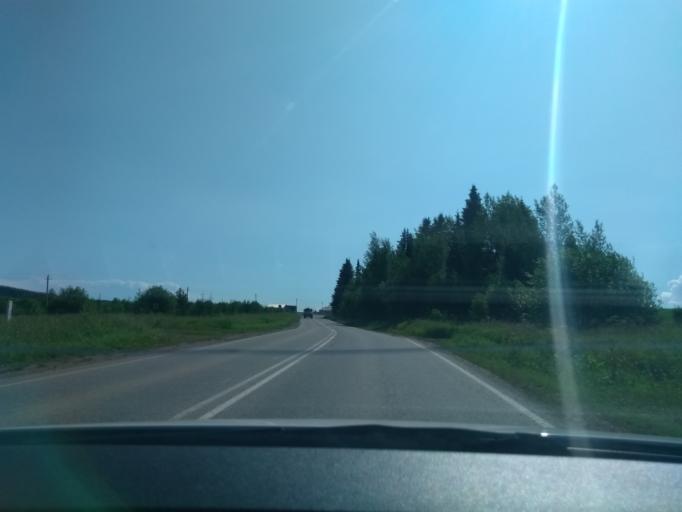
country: RU
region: Perm
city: Lobanovo
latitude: 57.8529
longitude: 56.3269
